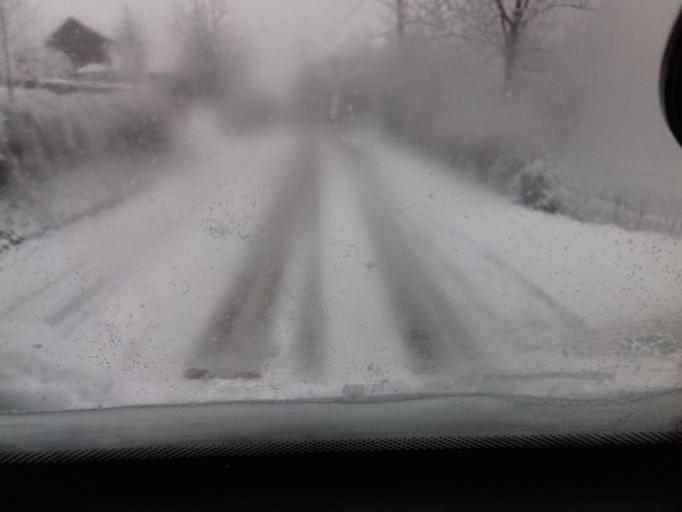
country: BA
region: Federation of Bosnia and Herzegovina
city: Lokvine
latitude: 44.2313
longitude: 17.8331
